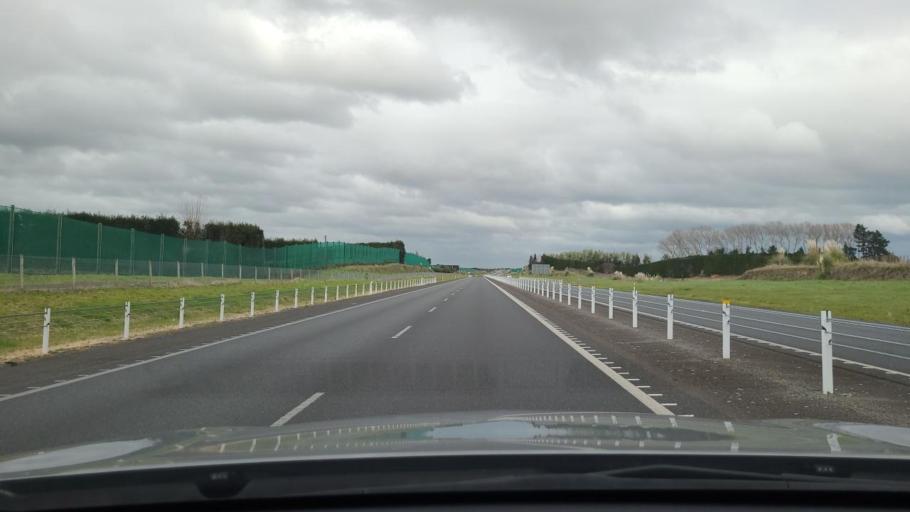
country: NZ
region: Bay of Plenty
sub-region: Western Bay of Plenty District
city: Maketu
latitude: -37.7827
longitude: 176.3878
